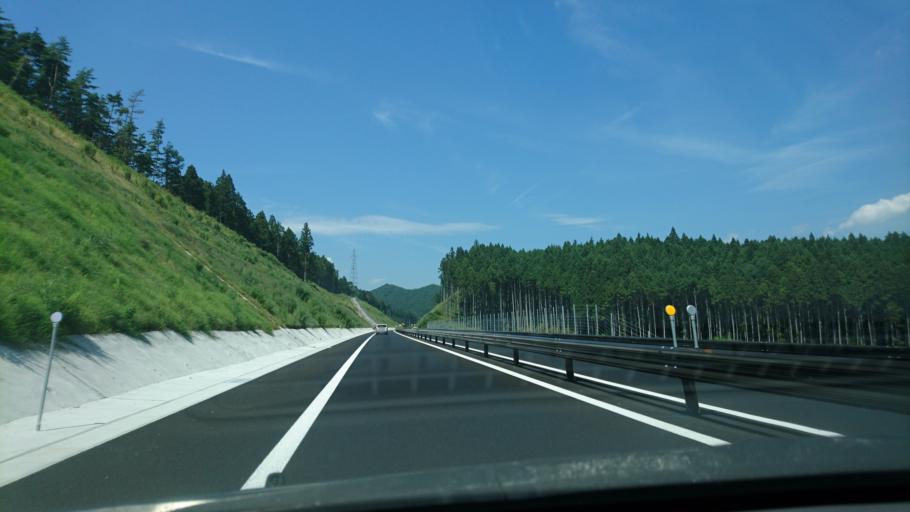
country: JP
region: Iwate
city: Ofunato
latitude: 39.0079
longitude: 141.6111
